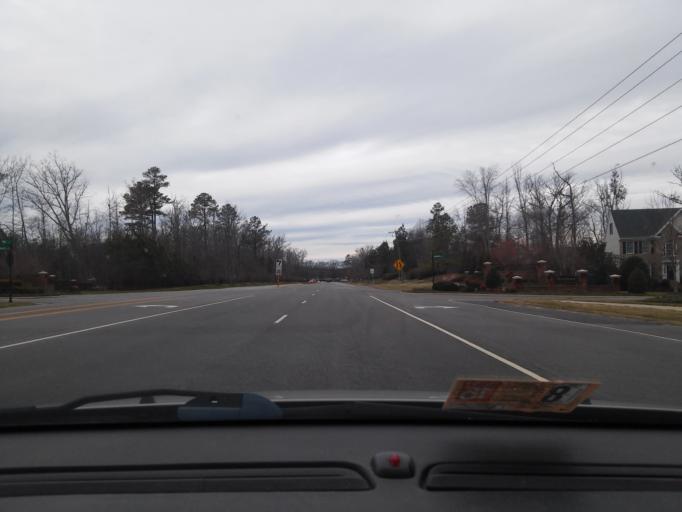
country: US
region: Virginia
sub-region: Chesterfield County
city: Bon Air
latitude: 37.5510
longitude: -77.6575
